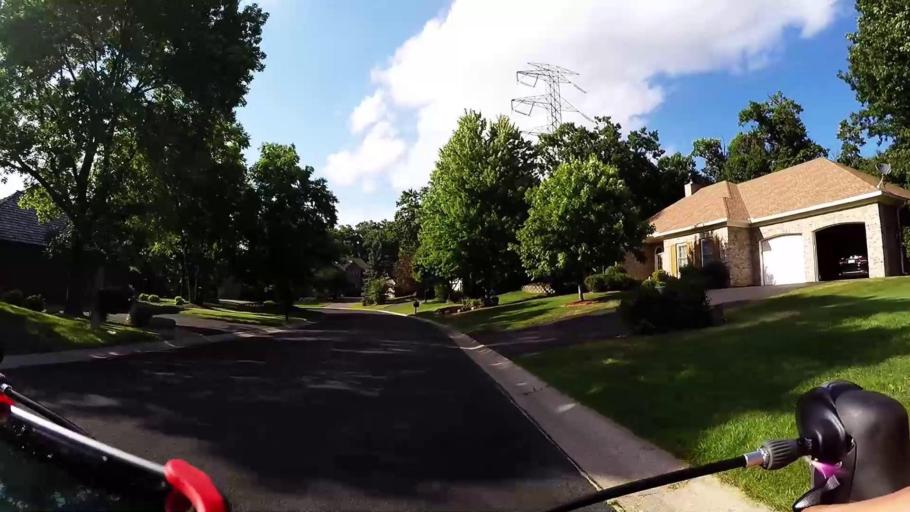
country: US
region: Minnesota
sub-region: Hennepin County
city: Eden Prairie
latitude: 44.8856
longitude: -93.4443
